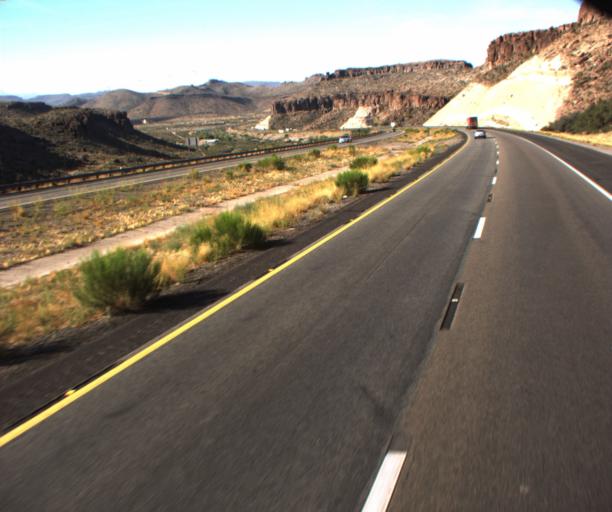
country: US
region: Arizona
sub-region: Mohave County
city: Kingman
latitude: 35.1779
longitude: -114.0742
